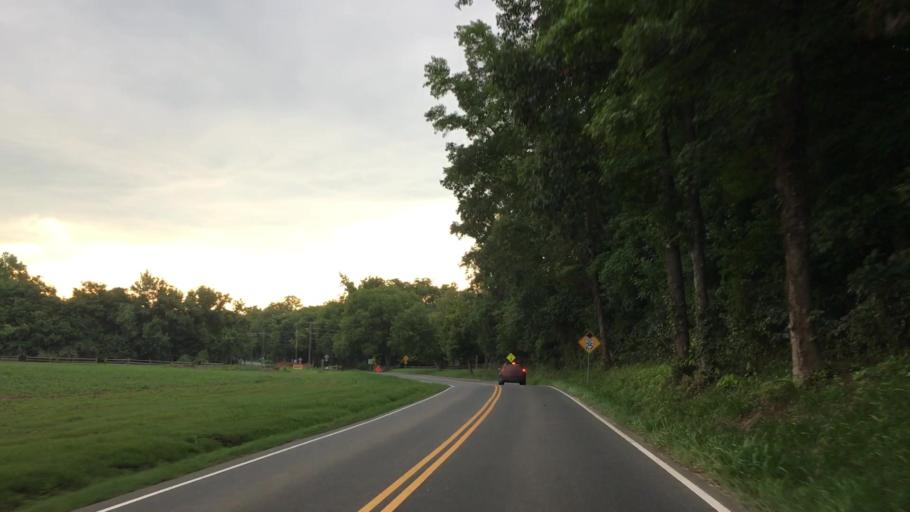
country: US
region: Virginia
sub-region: Stafford County
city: Falmouth
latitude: 38.3197
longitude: -77.4647
